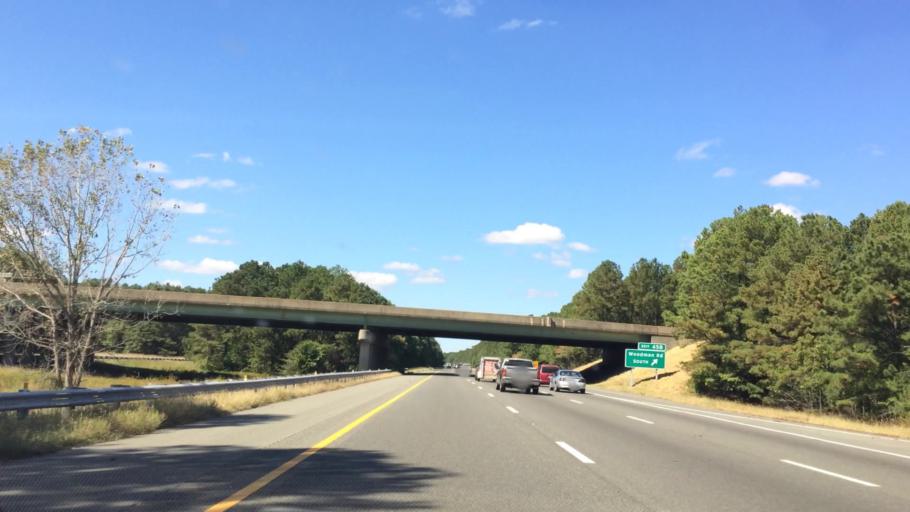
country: US
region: Virginia
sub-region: Henrico County
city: Glen Allen
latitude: 37.6669
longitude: -77.4835
